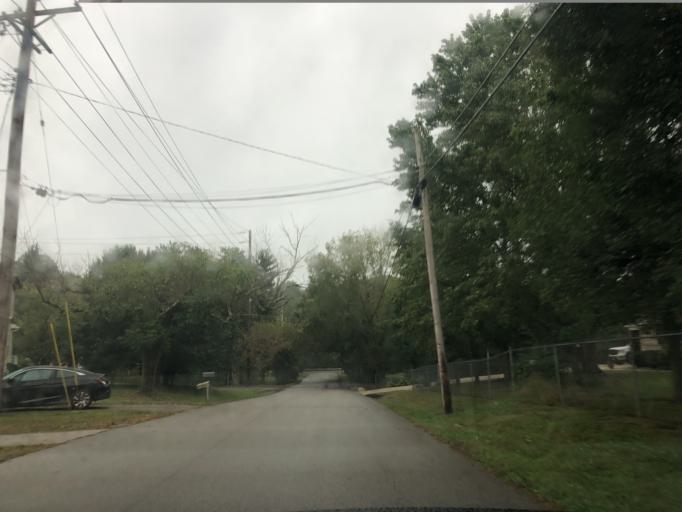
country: US
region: Ohio
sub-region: Hamilton County
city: The Village of Indian Hill
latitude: 39.2528
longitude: -84.2865
